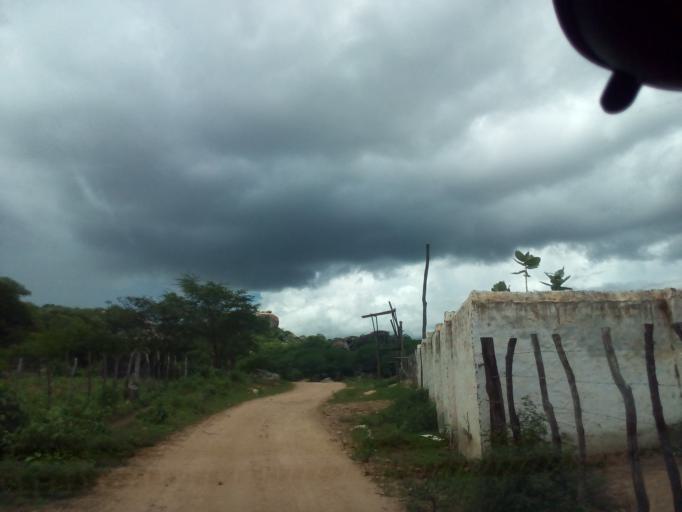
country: BR
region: Rio Grande do Norte
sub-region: Sao Tome
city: Sao Tome
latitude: -5.9507
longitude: -35.9242
